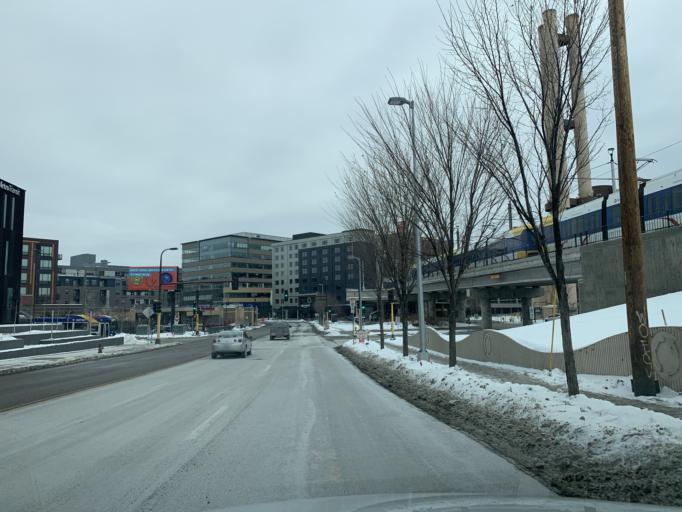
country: US
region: Minnesota
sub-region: Hennepin County
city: Minneapolis
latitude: 44.9844
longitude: -93.2815
